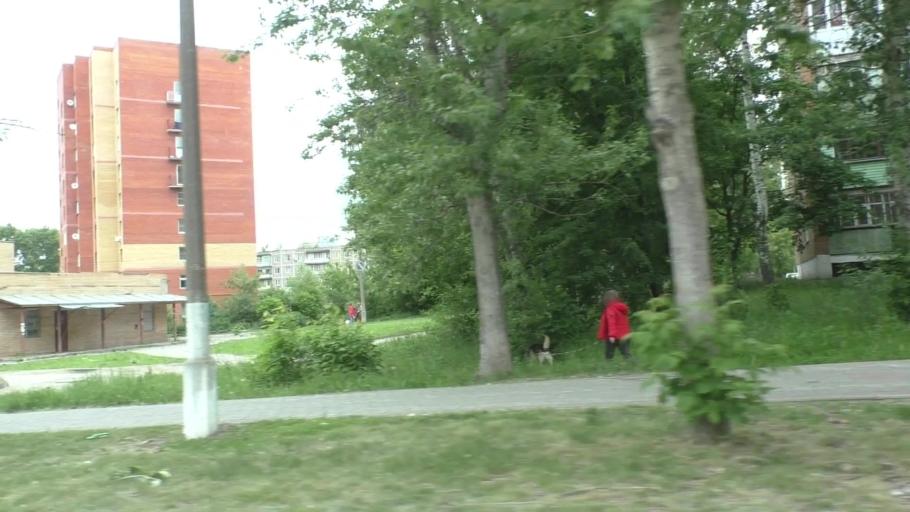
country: RU
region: Moskovskaya
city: Yegor'yevsk
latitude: 55.3670
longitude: 39.0565
